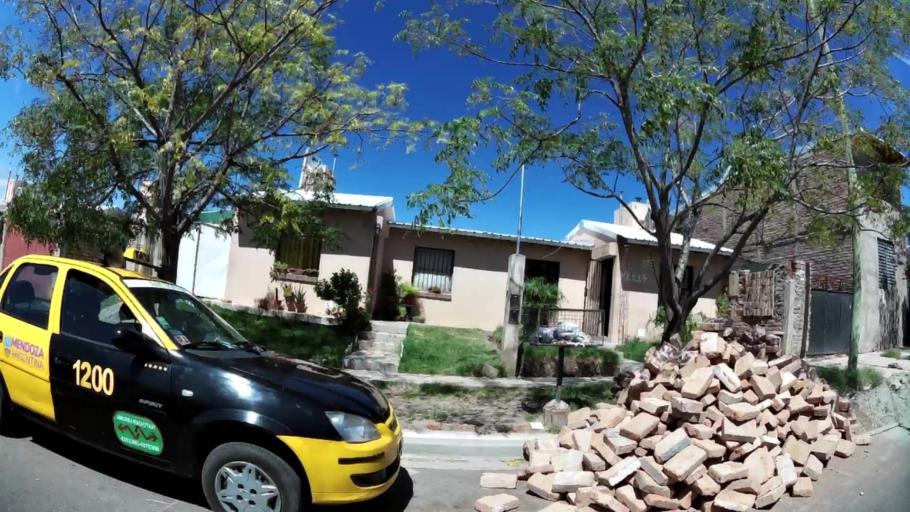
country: AR
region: Mendoza
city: Las Heras
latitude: -32.8523
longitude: -68.8729
